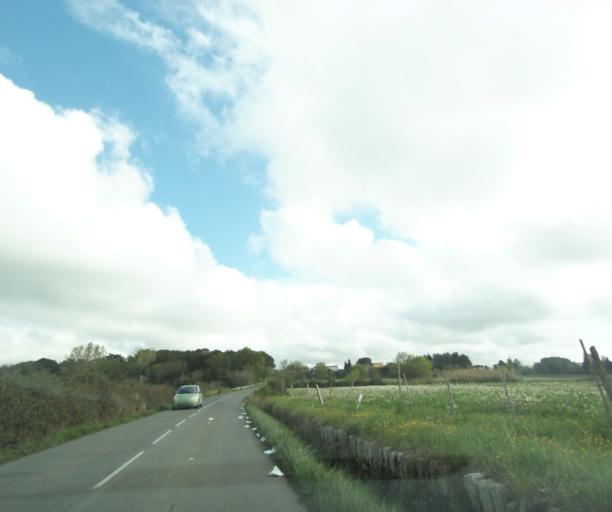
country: FR
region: Languedoc-Roussillon
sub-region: Departement de l'Herault
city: Saussan
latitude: 43.5760
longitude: 3.7708
